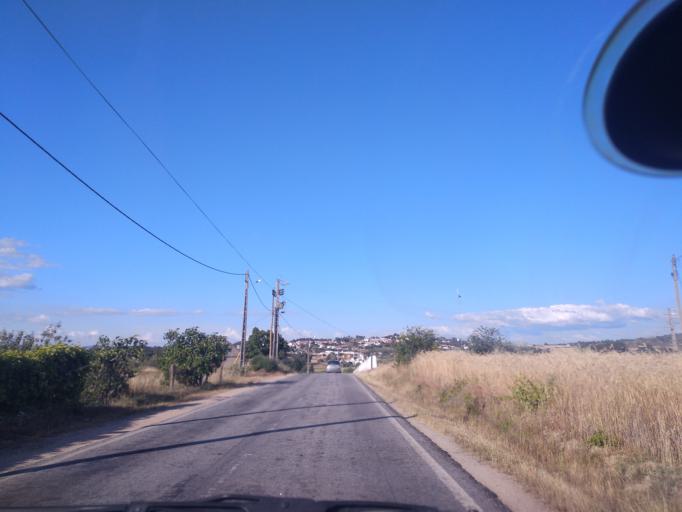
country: PT
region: Castelo Branco
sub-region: Covilha
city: Teixoso
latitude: 40.2498
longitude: -7.4064
